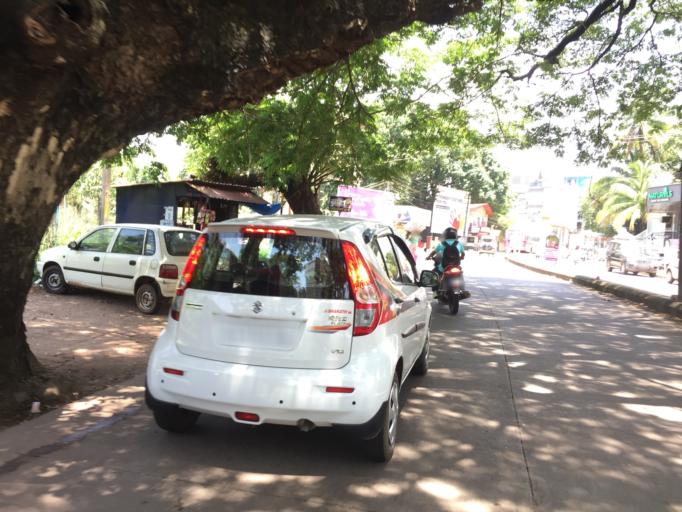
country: IN
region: Karnataka
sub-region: Dakshina Kannada
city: Mangalore
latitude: 12.8780
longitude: 74.8506
